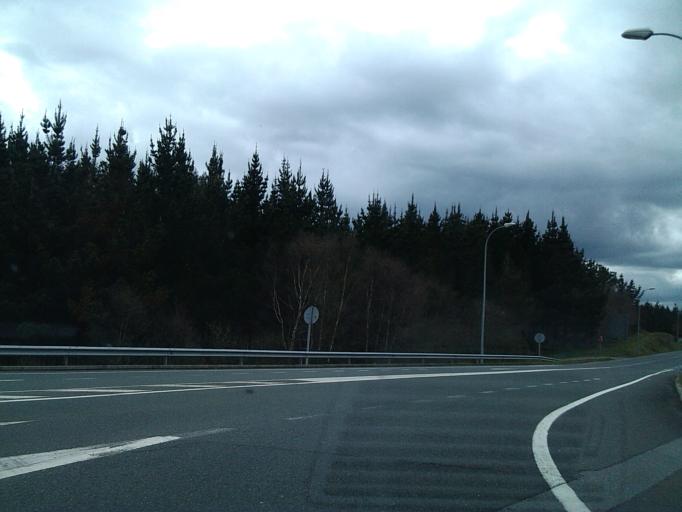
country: ES
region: Galicia
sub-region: Provincia de Lugo
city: Guitiriz
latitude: 43.1836
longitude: -7.8256
